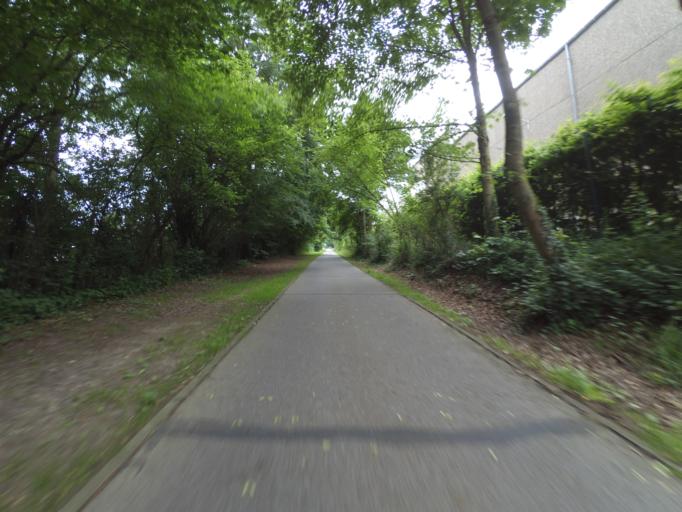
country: DE
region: North Rhine-Westphalia
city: Stolberg
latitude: 50.7406
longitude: 6.1602
